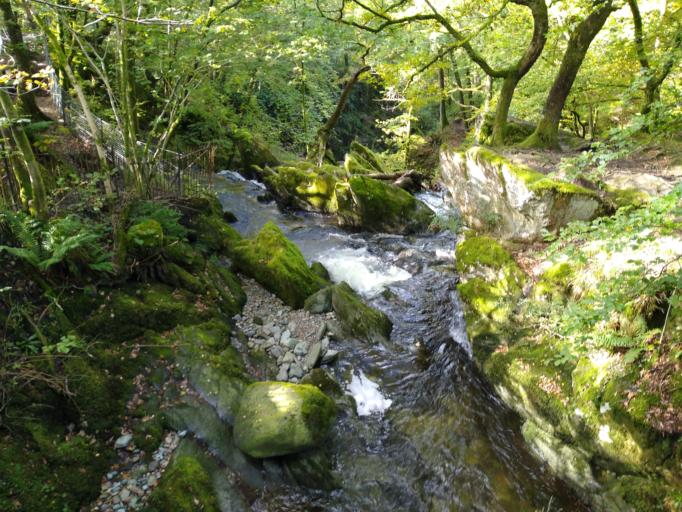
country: GB
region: England
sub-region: Cumbria
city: Ambleside
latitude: 54.4328
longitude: -2.9507
